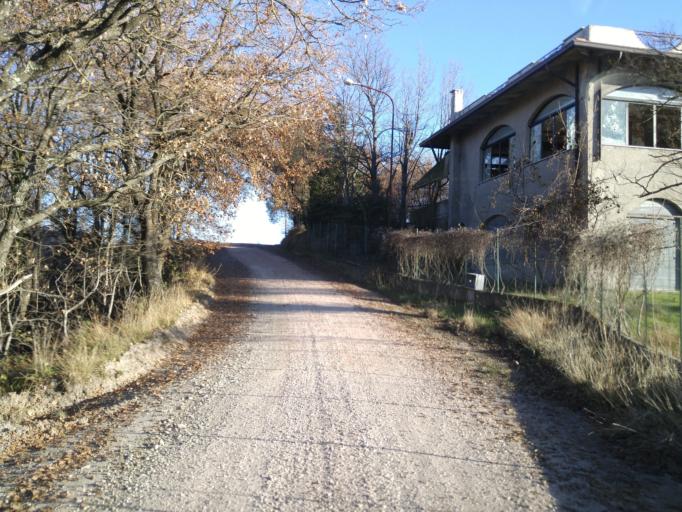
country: IT
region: The Marches
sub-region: Provincia di Pesaro e Urbino
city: Isola del Piano
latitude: 43.7719
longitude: 12.8057
